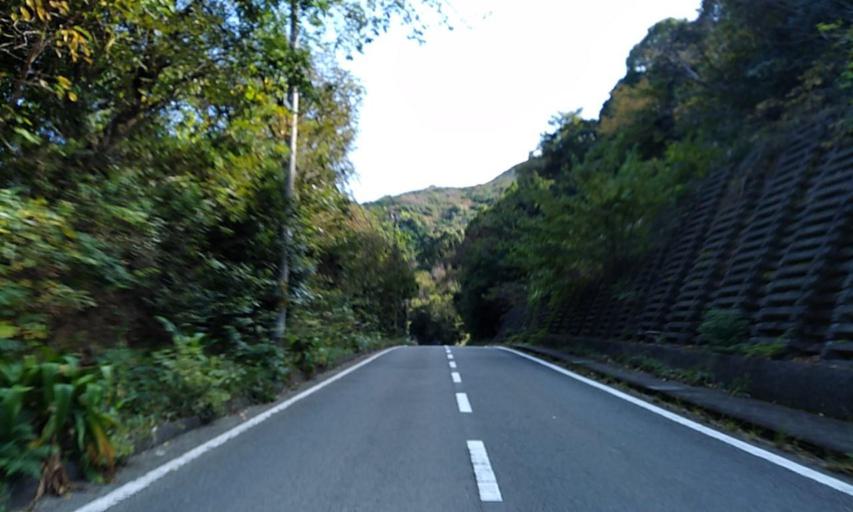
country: JP
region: Wakayama
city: Gobo
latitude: 33.9671
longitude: 135.0909
